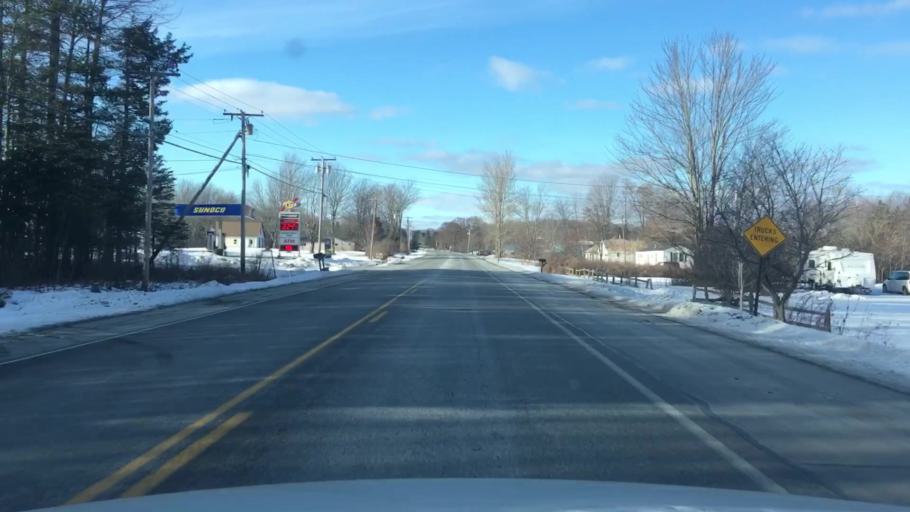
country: US
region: Maine
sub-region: Penobscot County
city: Eddington
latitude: 44.8230
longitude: -68.6512
